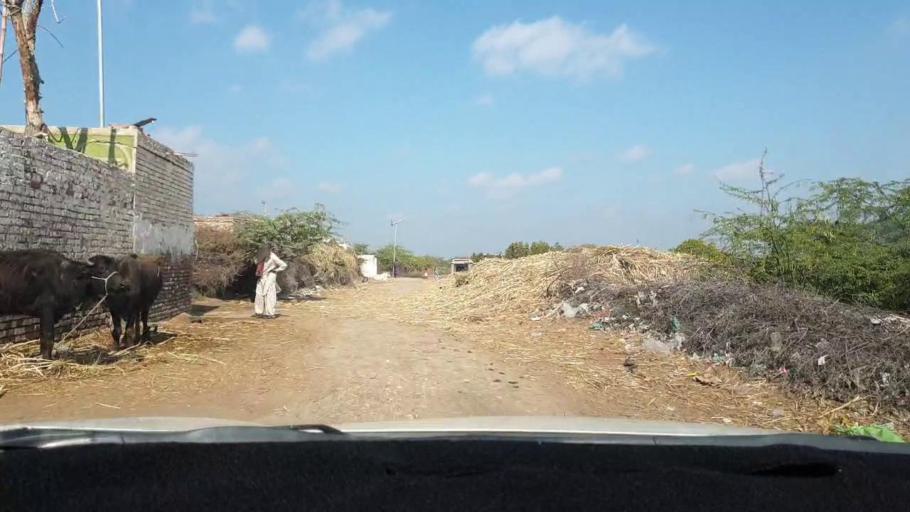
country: PK
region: Sindh
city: Berani
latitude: 25.7291
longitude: 68.9738
